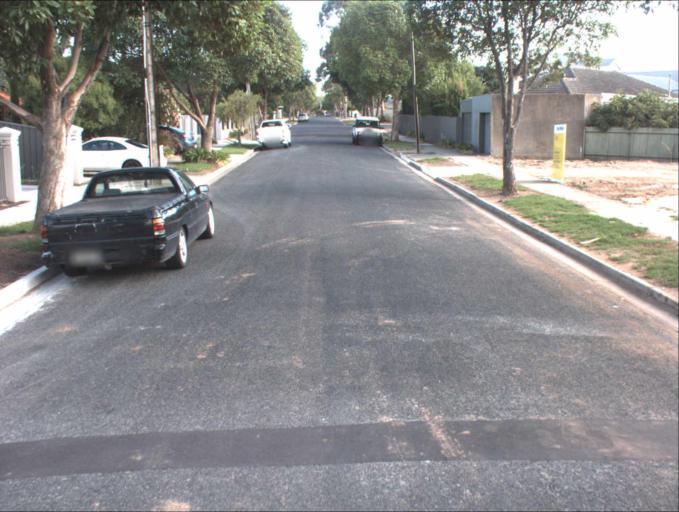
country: AU
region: South Australia
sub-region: Port Adelaide Enfield
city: Klemzig
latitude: -34.8774
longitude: 138.6259
